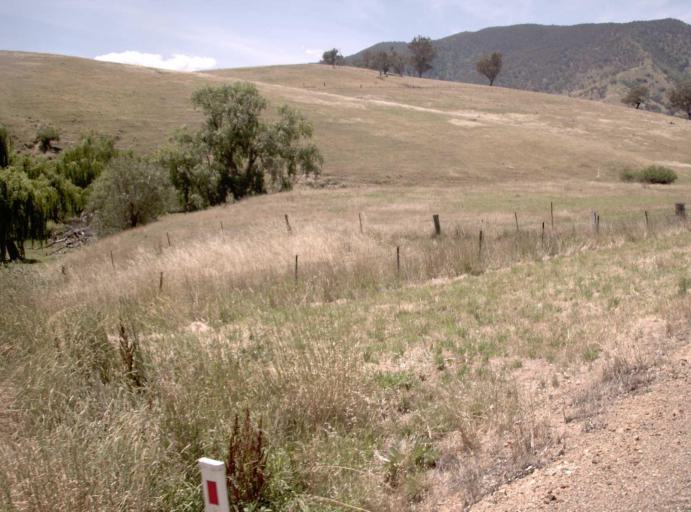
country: AU
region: Victoria
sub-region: East Gippsland
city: Bairnsdale
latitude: -37.1853
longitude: 147.7171
